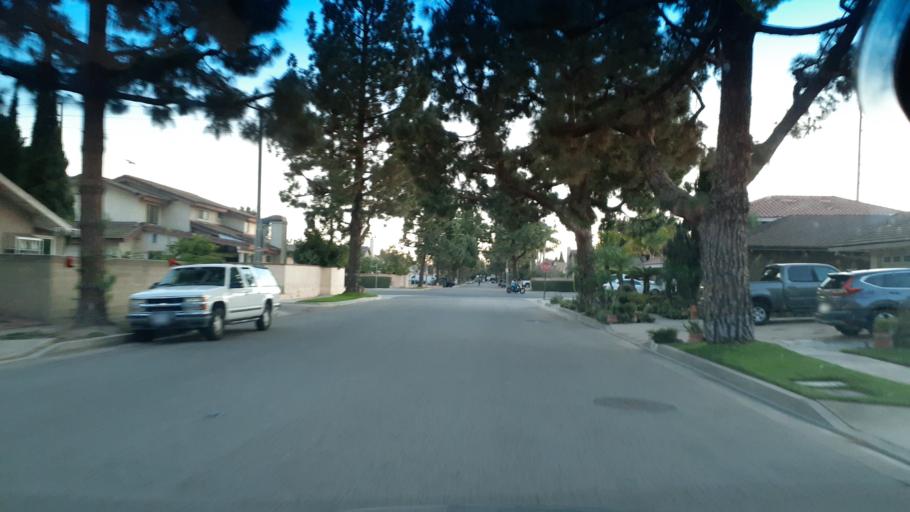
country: US
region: California
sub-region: Los Angeles County
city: Artesia
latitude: 33.8541
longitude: -118.0791
